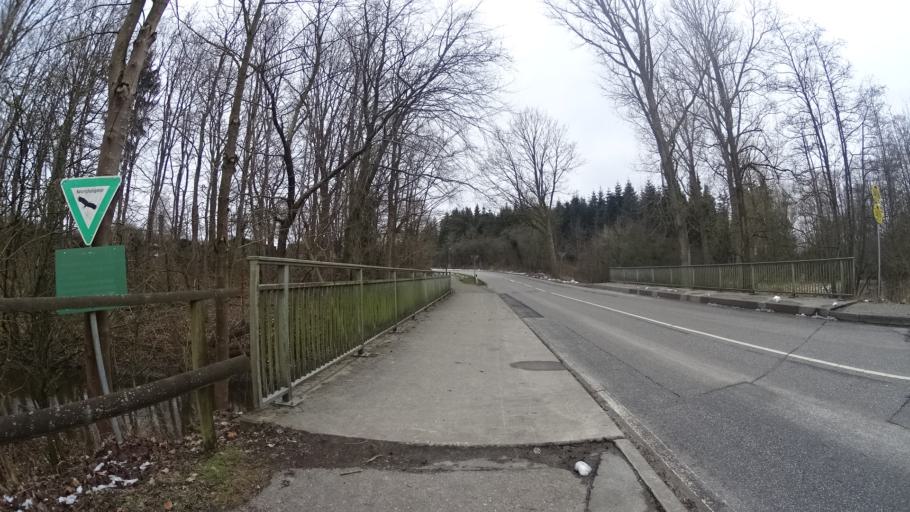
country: DE
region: Schleswig-Holstein
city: Lutjenburg
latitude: 54.2832
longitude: 10.5790
